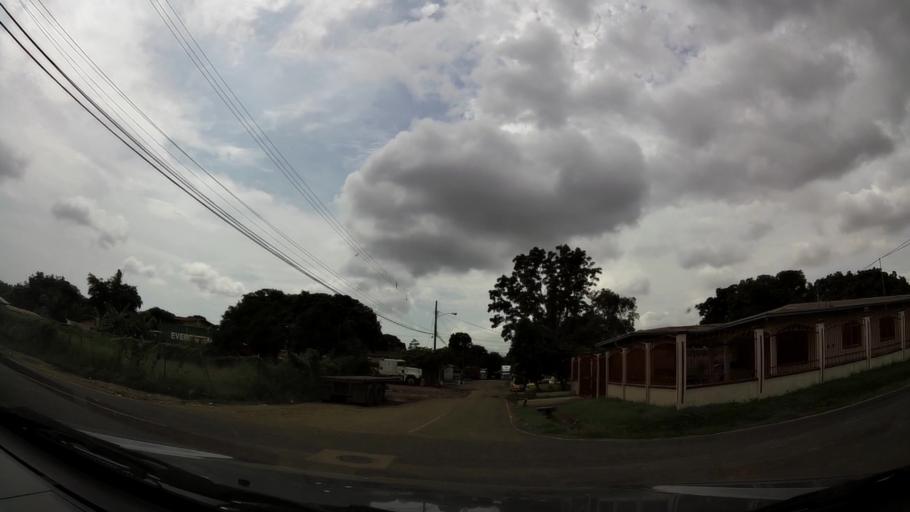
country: PA
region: Panama
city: San Miguelito
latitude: 9.0505
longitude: -79.4258
